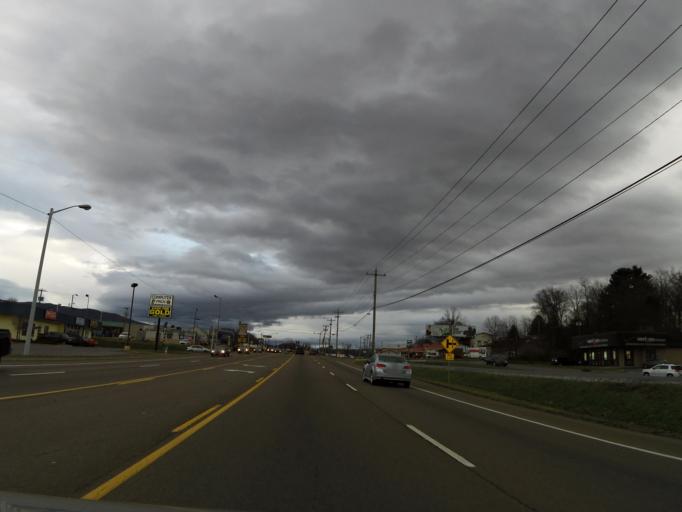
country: US
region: Tennessee
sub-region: Carter County
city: Elizabethton
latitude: 36.3502
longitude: -82.2365
